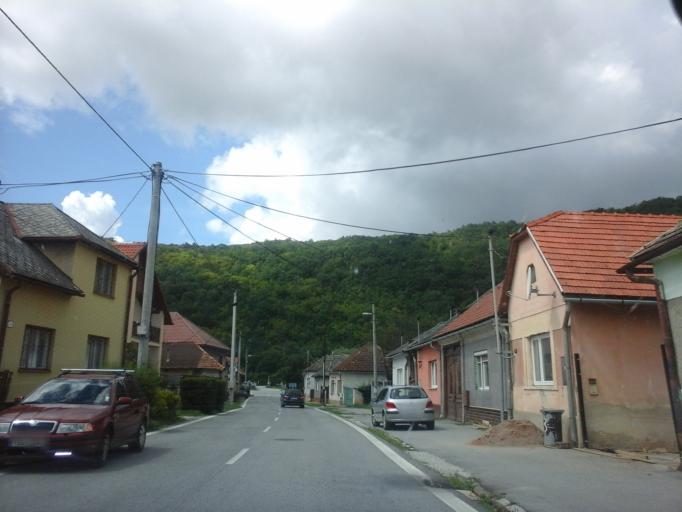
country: SK
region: Kosicky
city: Roznava
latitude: 48.5462
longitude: 20.3996
